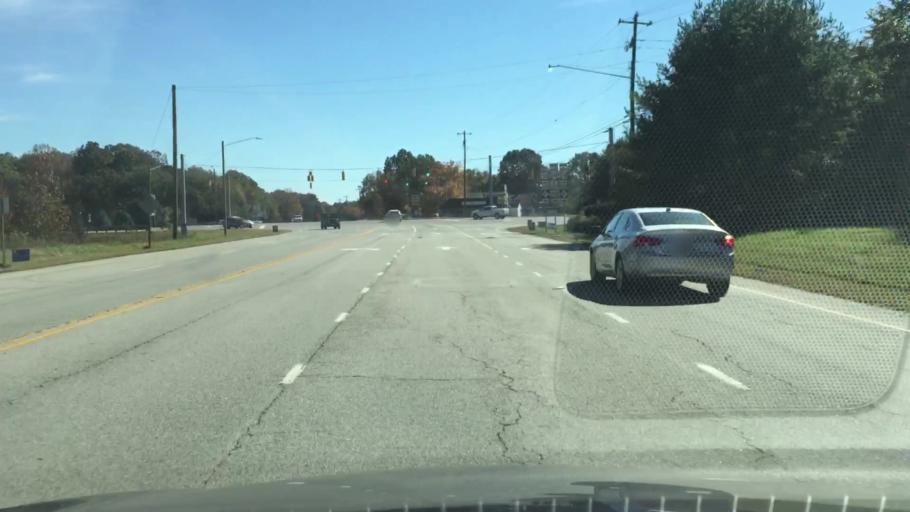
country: US
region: North Carolina
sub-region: Rockingham County
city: Reidsville
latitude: 36.3158
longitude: -79.6726
